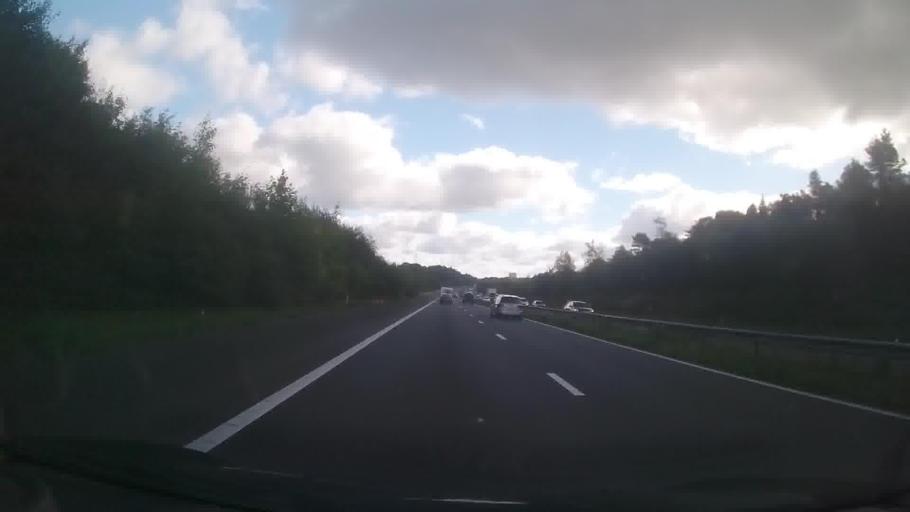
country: GB
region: Wales
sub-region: City and County of Swansea
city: Pontlliw
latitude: 51.6766
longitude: -3.9946
